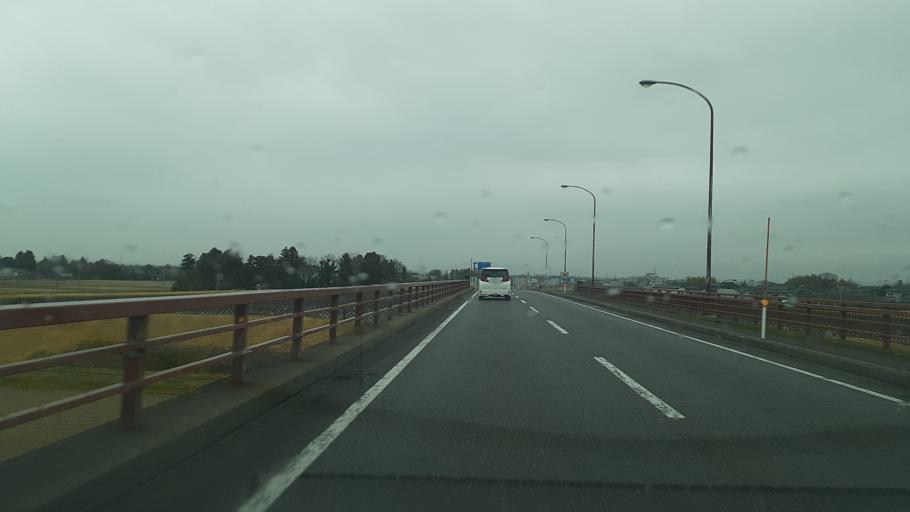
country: JP
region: Niigata
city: Kameda-honcho
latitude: 37.8810
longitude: 139.1684
